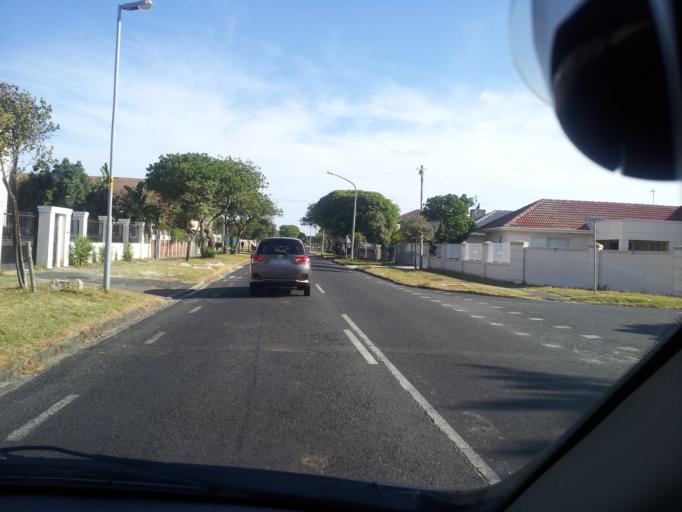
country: ZA
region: Western Cape
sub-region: City of Cape Town
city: Rosebank
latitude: -33.9198
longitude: 18.5350
